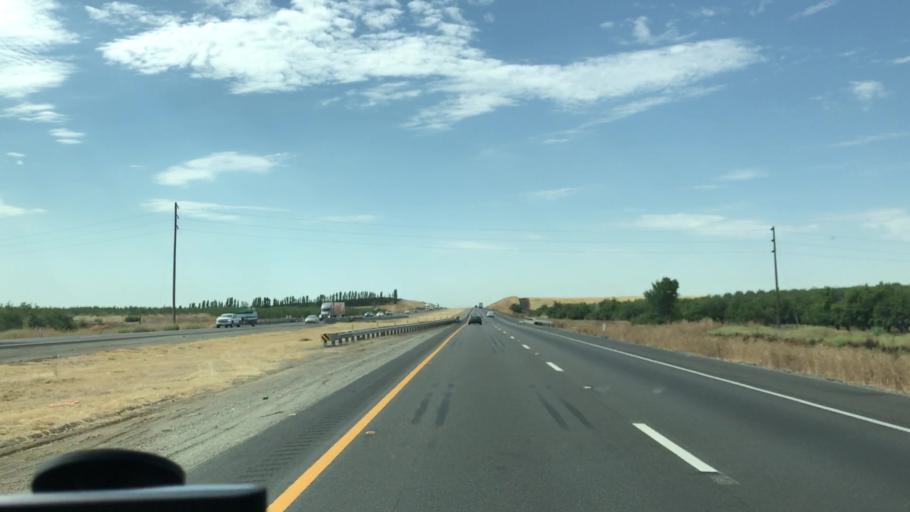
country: US
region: California
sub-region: Stanislaus County
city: Patterson
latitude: 37.3752
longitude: -121.1263
